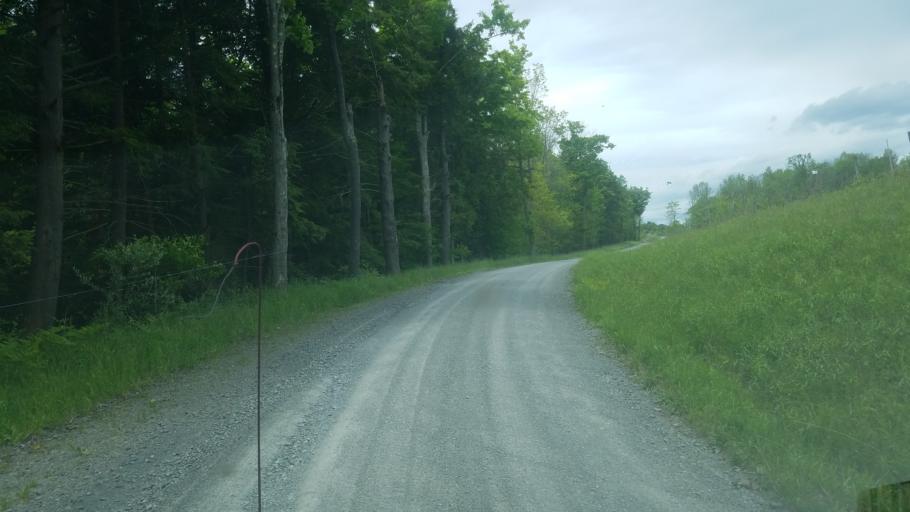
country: US
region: Pennsylvania
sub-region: Tioga County
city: Westfield
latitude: 41.8415
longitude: -77.6025
